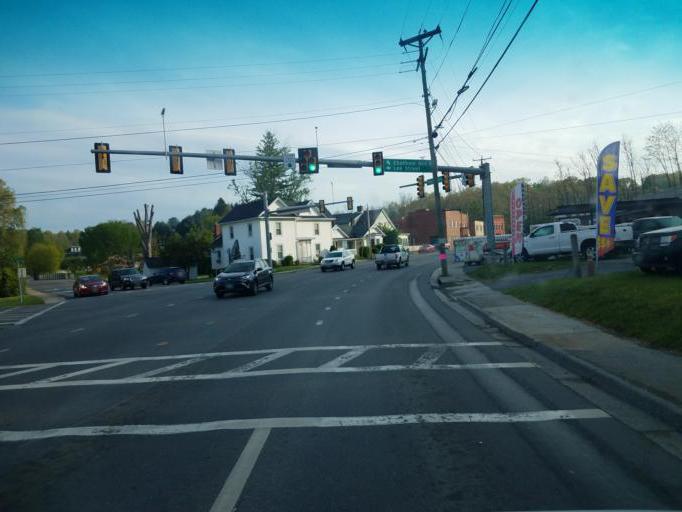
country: US
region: Virginia
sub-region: Smyth County
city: Marion
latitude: 36.8363
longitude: -81.5158
